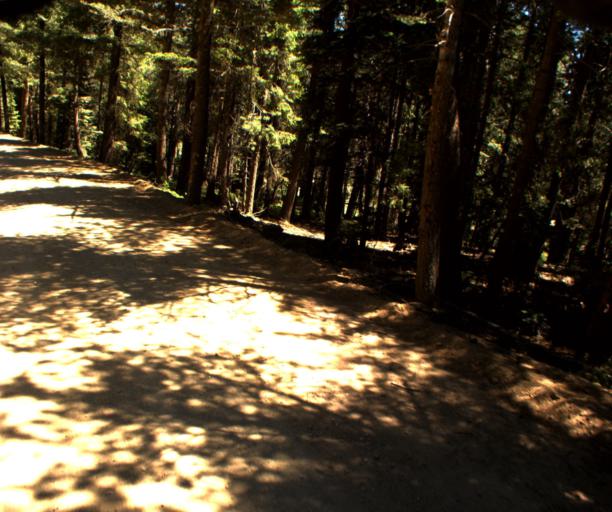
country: US
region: Arizona
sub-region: Graham County
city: Swift Trail Junction
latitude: 32.6670
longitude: -109.8760
